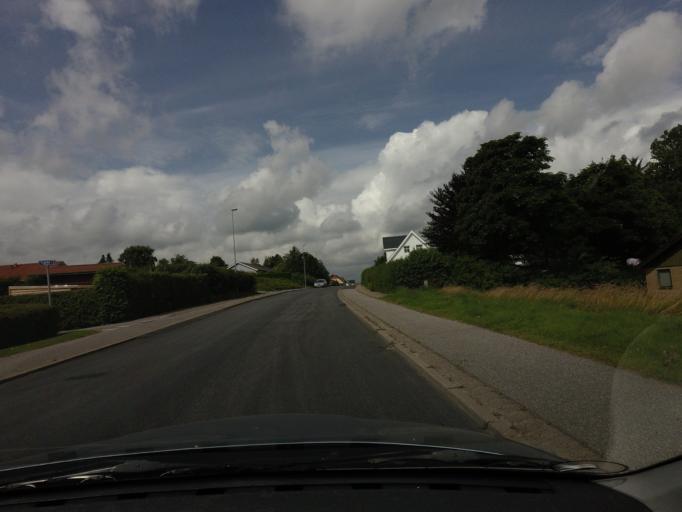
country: DK
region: North Denmark
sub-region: Hjorring Kommune
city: Tars
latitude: 57.3829
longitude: 10.1241
